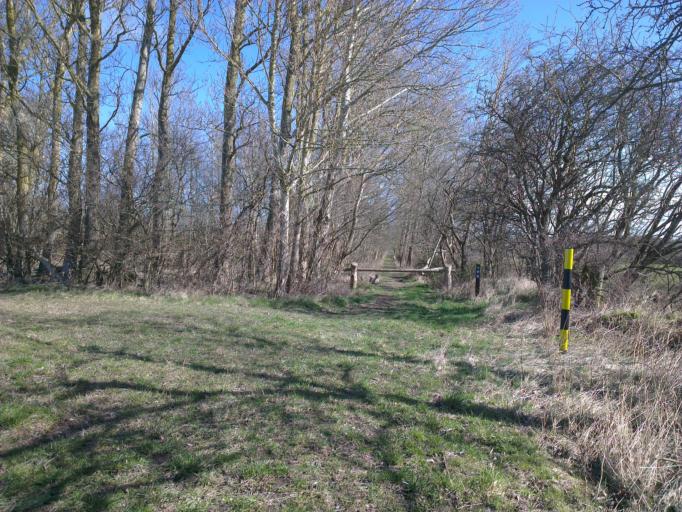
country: DK
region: Capital Region
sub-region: Frederikssund Kommune
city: Jaegerspris
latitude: 55.8713
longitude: 11.9748
